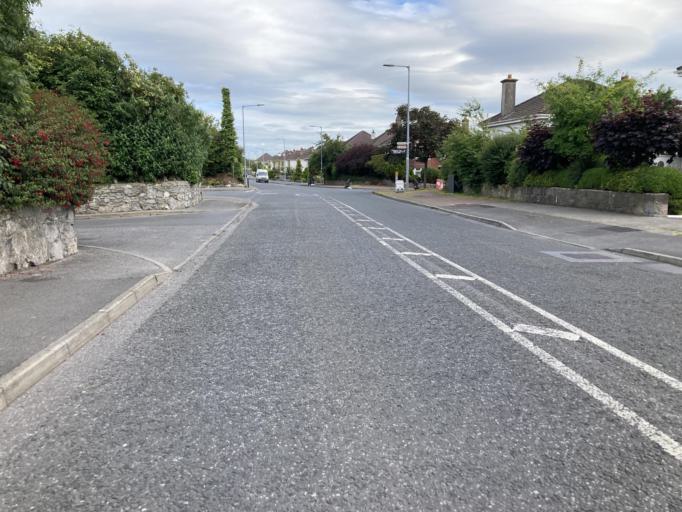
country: IE
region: Connaught
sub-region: County Galway
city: Bearna
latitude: 53.2623
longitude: -9.1255
